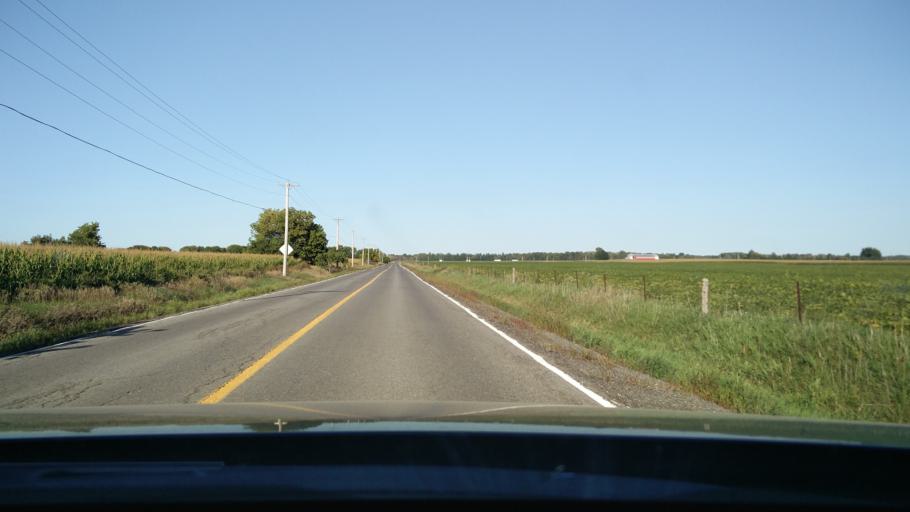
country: CA
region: Ontario
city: Bells Corners
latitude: 45.2090
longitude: -75.7931
